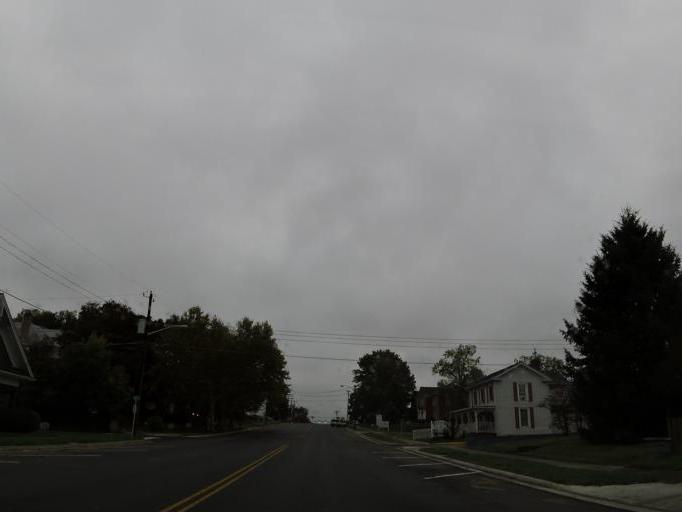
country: US
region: Virginia
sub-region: Wythe County
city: Wytheville
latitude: 36.9473
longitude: -81.0868
